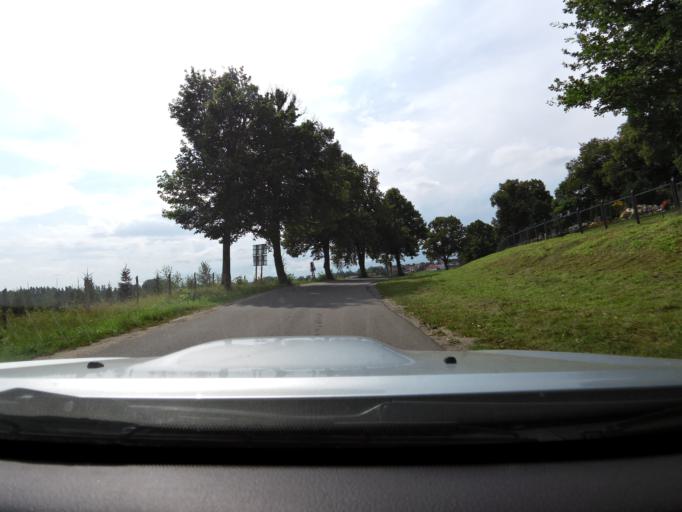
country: PL
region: Warmian-Masurian Voivodeship
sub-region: Powiat ketrzynski
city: Ketrzyn
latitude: 54.0811
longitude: 21.4320
